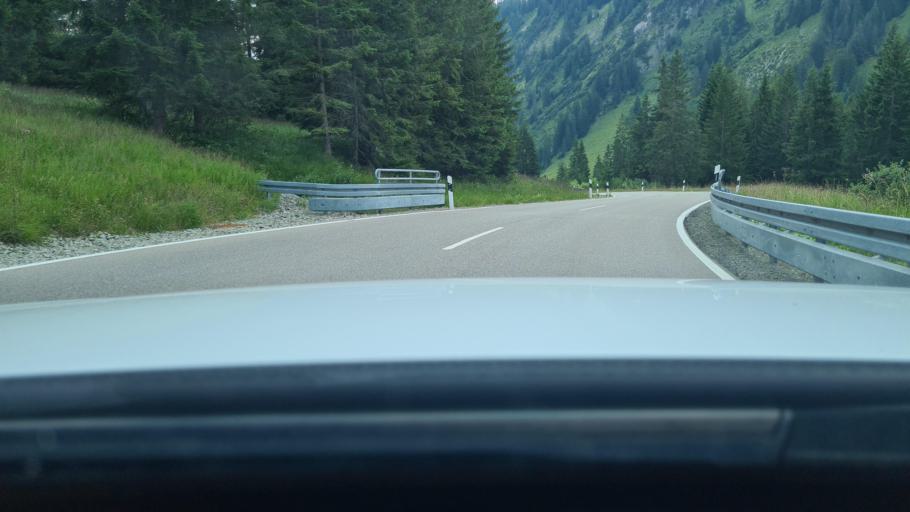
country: DE
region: Bavaria
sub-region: Swabia
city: Obermaiselstein
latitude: 47.4348
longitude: 10.1830
